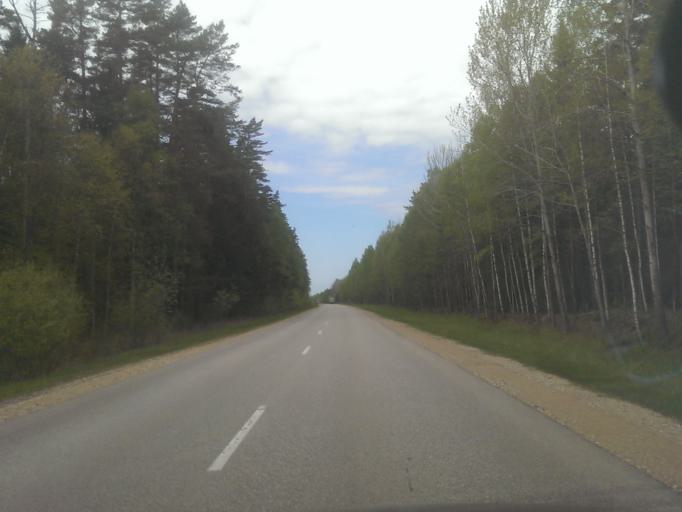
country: LV
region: Ventspils Rajons
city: Piltene
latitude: 57.1612
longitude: 21.6904
